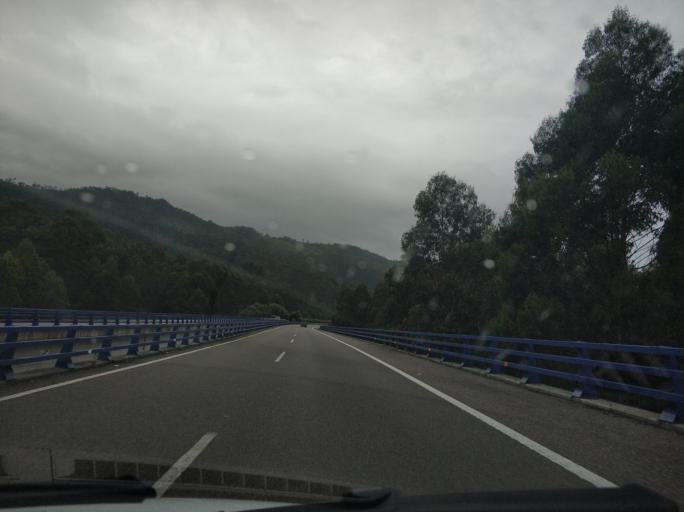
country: ES
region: Galicia
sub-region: Provincia de Lugo
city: Ribadeo
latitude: 43.5352
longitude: -7.1338
